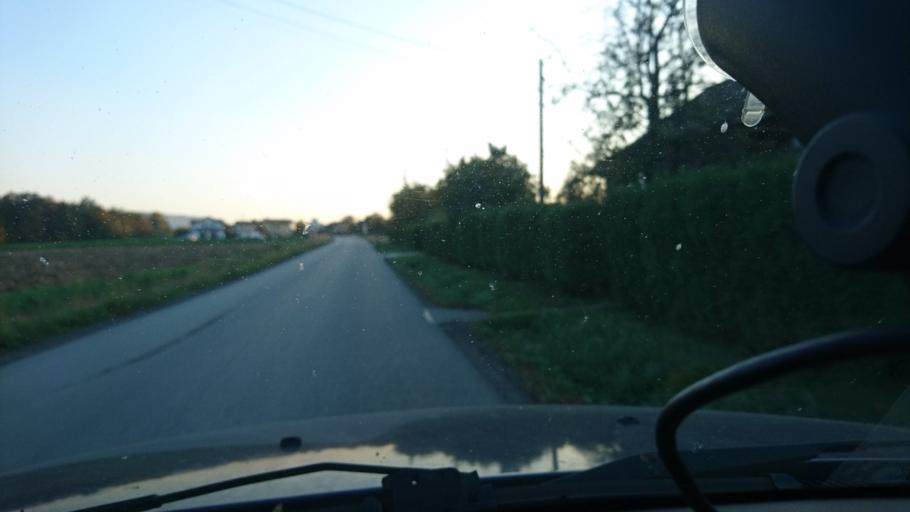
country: PL
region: Silesian Voivodeship
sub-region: Powiat bielski
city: Pisarzowice
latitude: 49.8696
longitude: 19.1398
